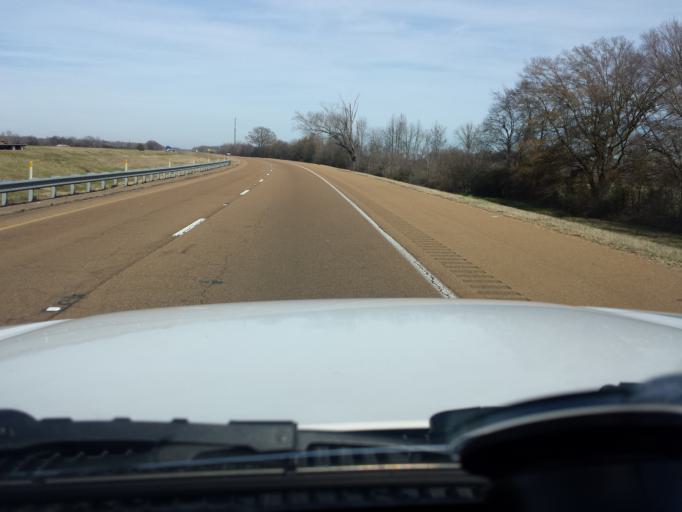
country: US
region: Mississippi
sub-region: Madison County
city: Canton
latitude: 32.6242
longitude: -90.0626
